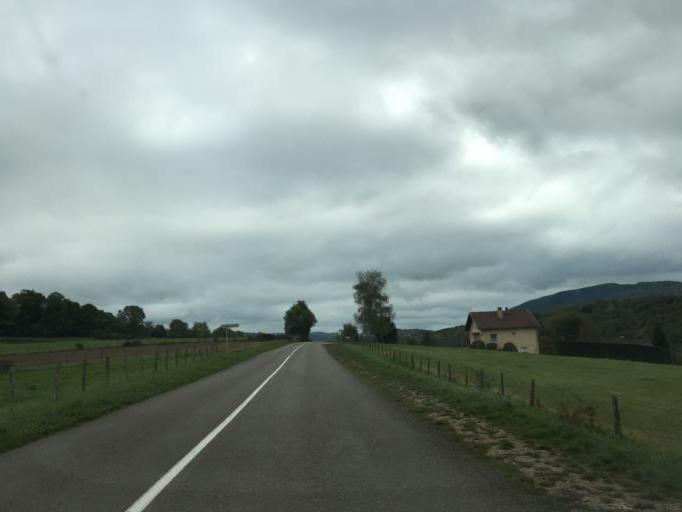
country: FR
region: Rhone-Alpes
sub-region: Departement de l'Ain
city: Cuisiat
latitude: 46.3583
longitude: 5.4358
